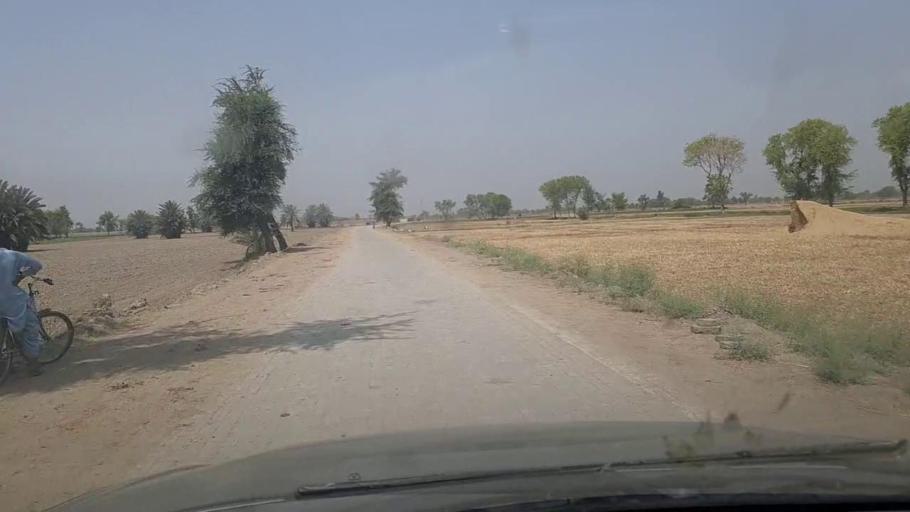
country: PK
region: Sindh
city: Adilpur
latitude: 27.9389
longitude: 69.3144
